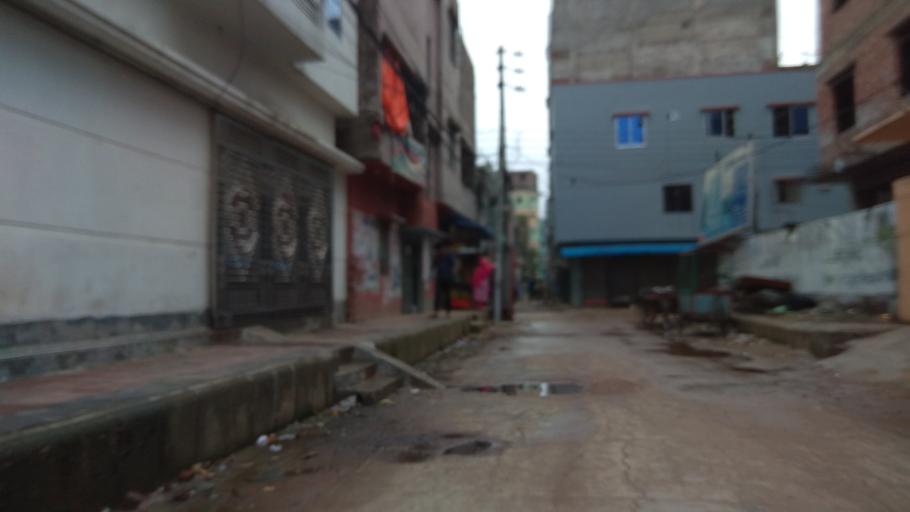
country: BD
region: Dhaka
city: Tungi
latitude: 23.8207
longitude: 90.3760
